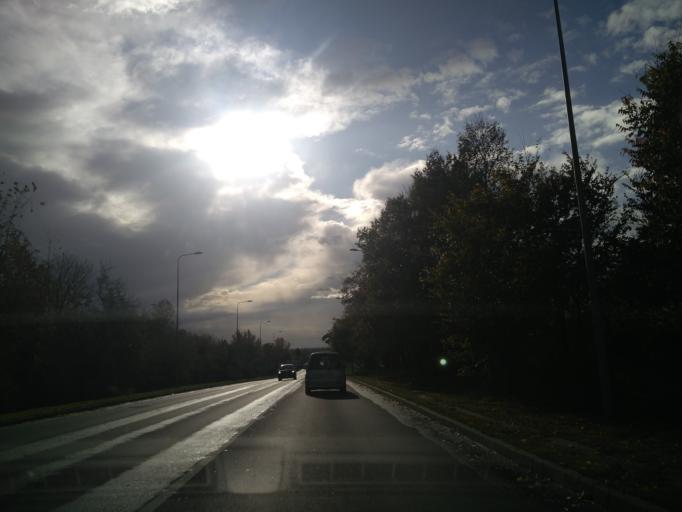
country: HU
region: Pest
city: Csomor
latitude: 47.5335
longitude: 19.2406
